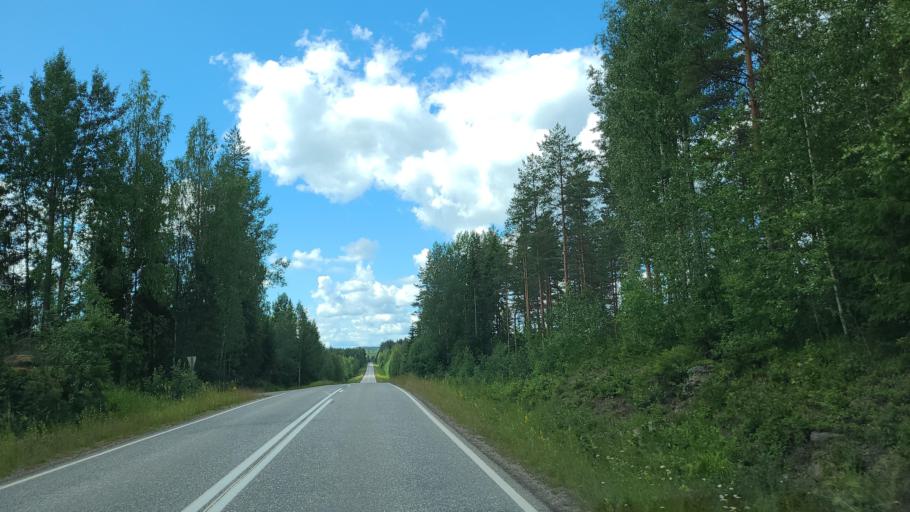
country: FI
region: Northern Savo
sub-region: Koillis-Savo
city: Kaavi
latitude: 62.9828
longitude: 28.8072
